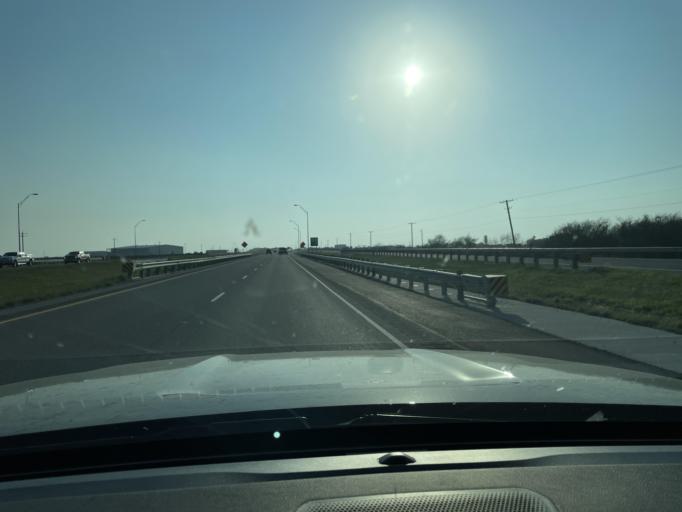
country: US
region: Texas
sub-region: Nueces County
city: Robstown
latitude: 27.7474
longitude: -97.6940
